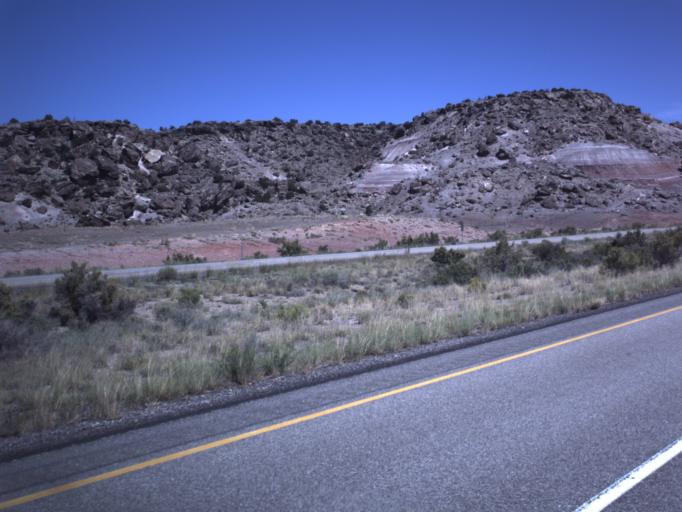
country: US
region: Utah
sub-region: Emery County
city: Ferron
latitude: 38.8176
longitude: -111.1657
